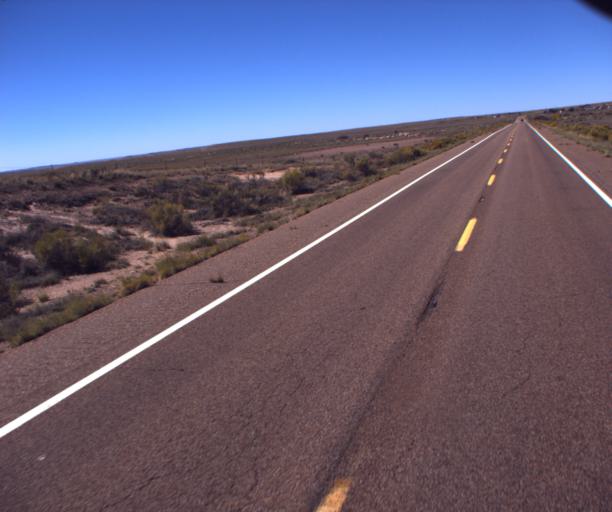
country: US
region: Arizona
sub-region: Navajo County
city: Holbrook
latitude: 34.7873
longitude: -109.8765
